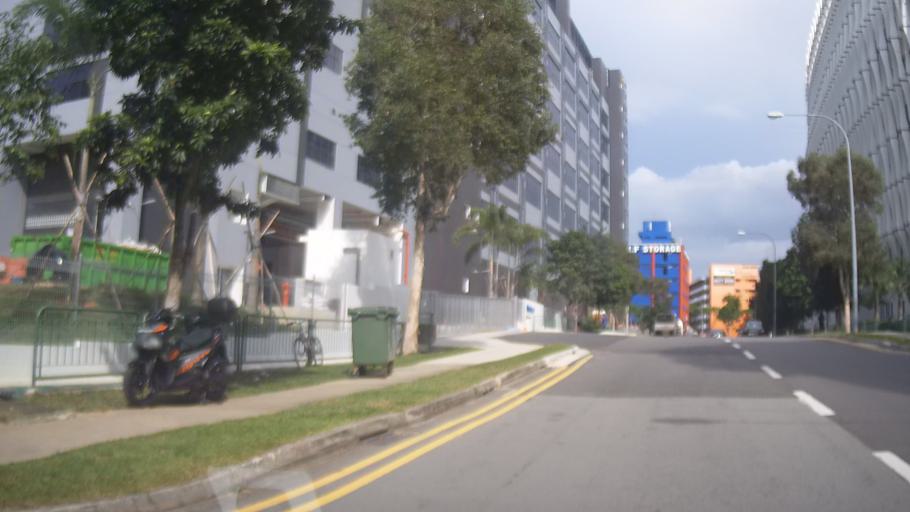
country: SG
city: Singapore
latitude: 1.3251
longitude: 103.8731
